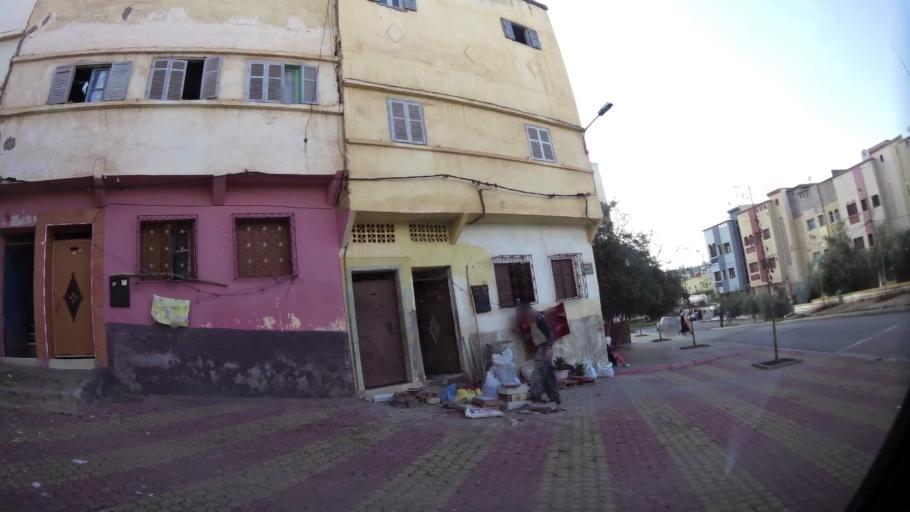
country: MA
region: Chaouia-Ouardigha
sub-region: Settat Province
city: Settat
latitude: 33.0079
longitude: -7.6287
